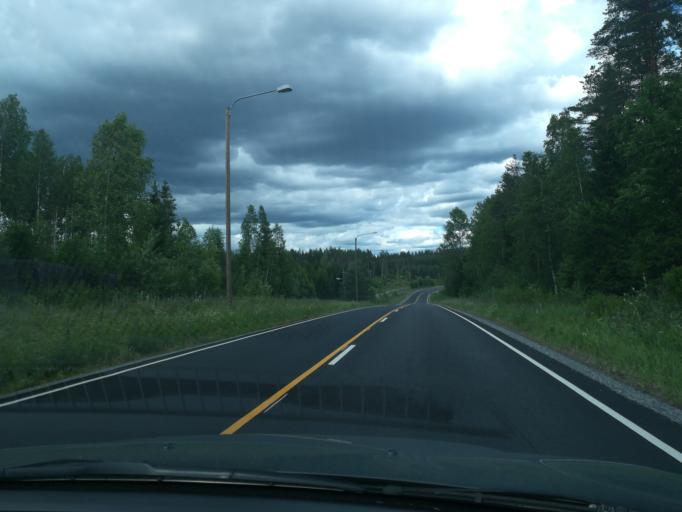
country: FI
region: Southern Savonia
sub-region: Mikkeli
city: Mikkeli
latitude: 61.6584
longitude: 27.1042
